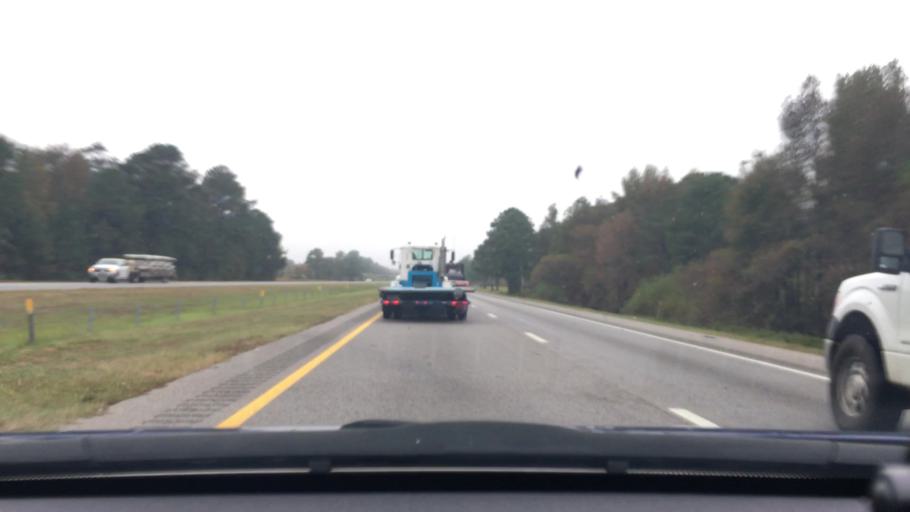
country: US
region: South Carolina
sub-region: Lee County
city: Bishopville
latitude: 34.1889
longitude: -80.2416
